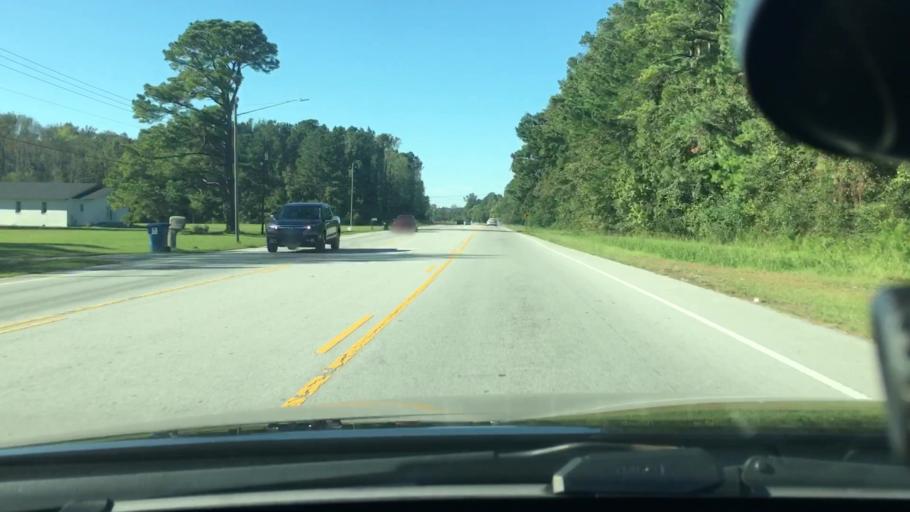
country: US
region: North Carolina
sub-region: Craven County
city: Trent Woods
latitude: 35.1528
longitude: -77.1106
